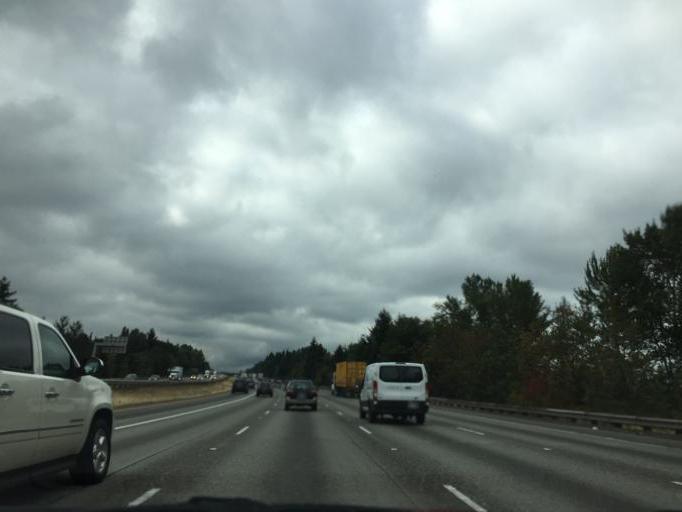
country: US
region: Washington
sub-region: King County
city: SeaTac
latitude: 47.4172
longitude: -122.2896
